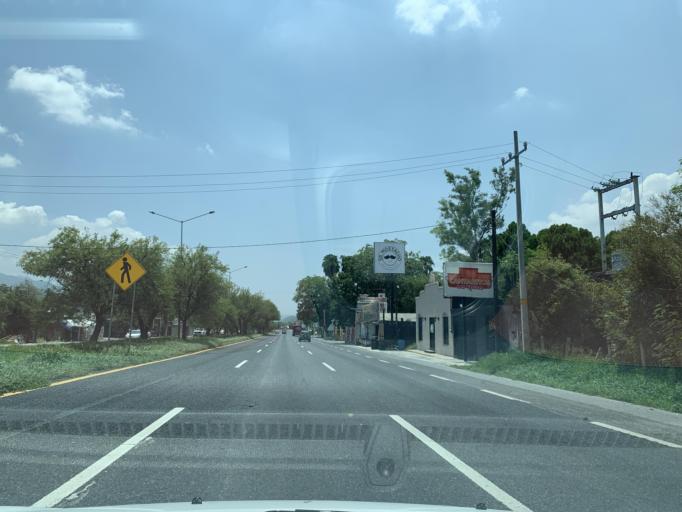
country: MX
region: Nuevo Leon
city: Santiago
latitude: 25.4652
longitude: -100.1726
